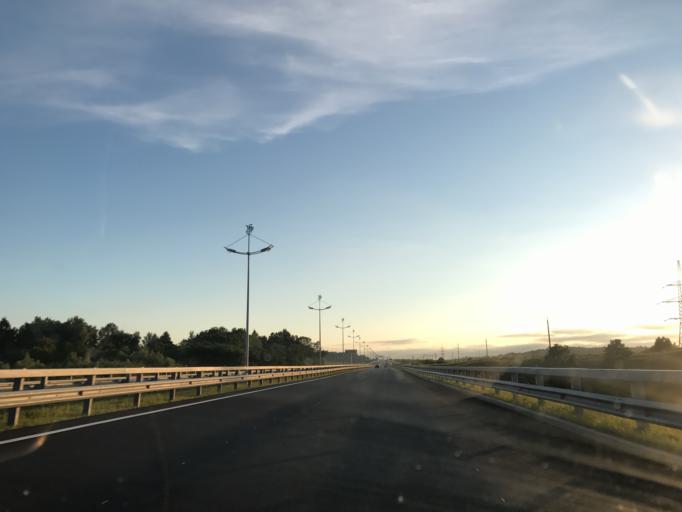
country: RU
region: Kaliningrad
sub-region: Gorod Kaliningrad
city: Pionerskiy
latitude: 54.9211
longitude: 20.2950
